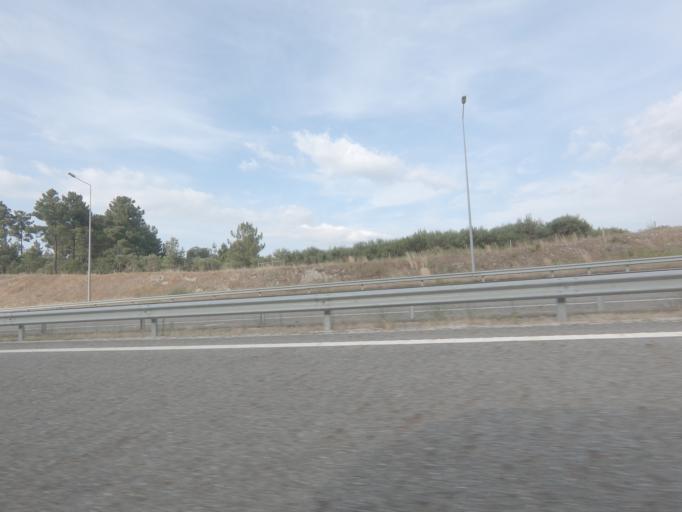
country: PT
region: Vila Real
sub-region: Chaves
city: Chaves
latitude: 41.7185
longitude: -7.5429
